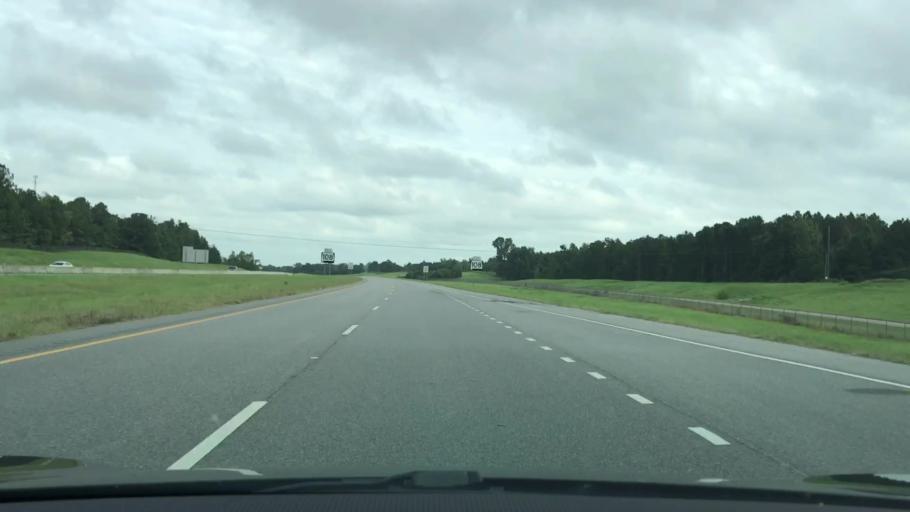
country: US
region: Alabama
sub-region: Montgomery County
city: Pike Road
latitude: 32.3436
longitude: -86.0637
